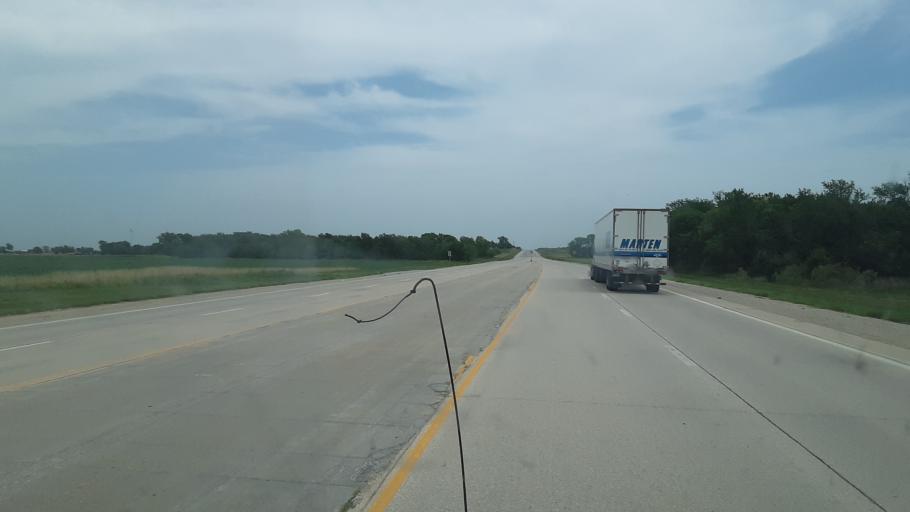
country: US
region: Kansas
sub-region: Allen County
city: Iola
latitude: 37.9220
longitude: -95.2951
